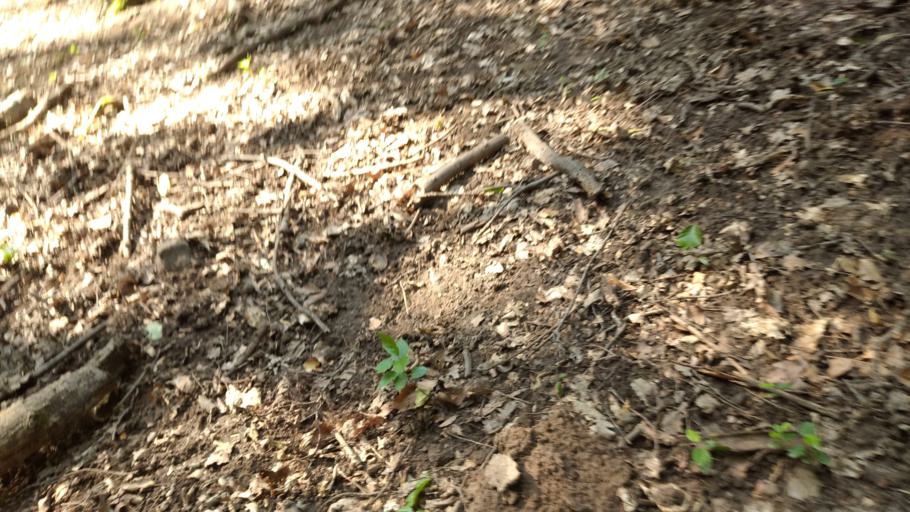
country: HU
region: Pest
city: Nagymaros
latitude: 47.7853
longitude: 18.9269
